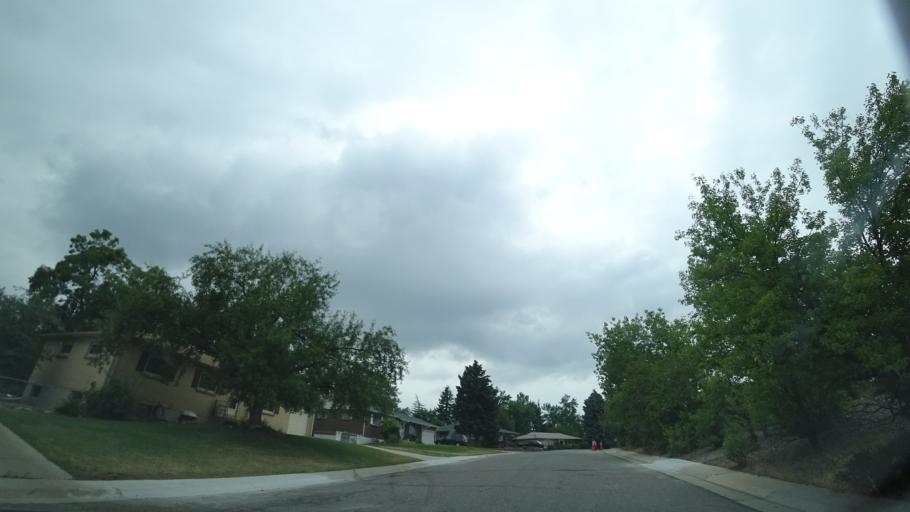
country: US
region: Colorado
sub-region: Jefferson County
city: Lakewood
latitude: 39.7005
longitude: -105.1298
